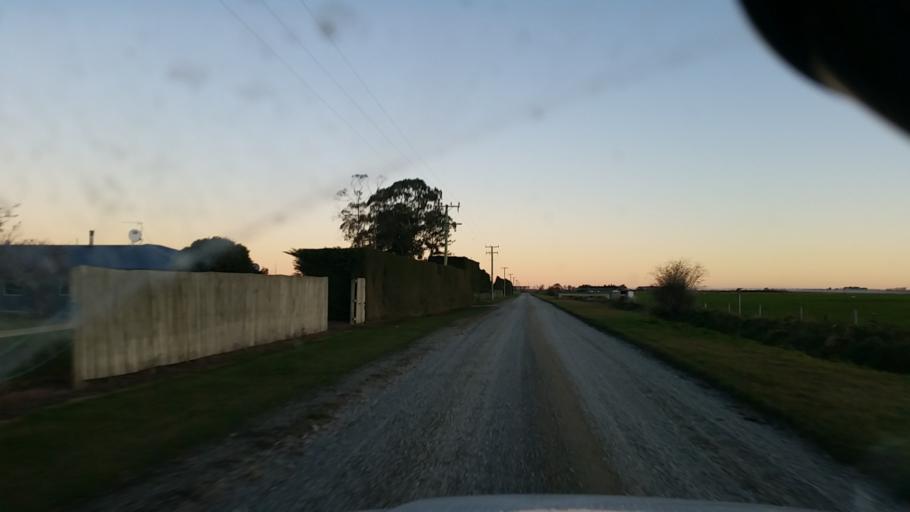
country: NZ
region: Canterbury
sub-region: Ashburton District
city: Tinwald
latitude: -44.0469
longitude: 171.6633
